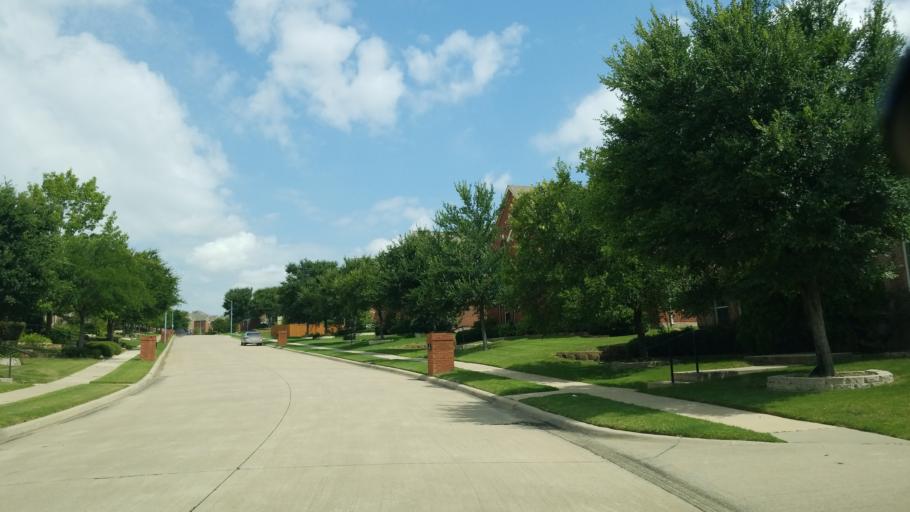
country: US
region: Texas
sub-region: Dallas County
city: Coppell
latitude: 32.9281
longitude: -96.9617
